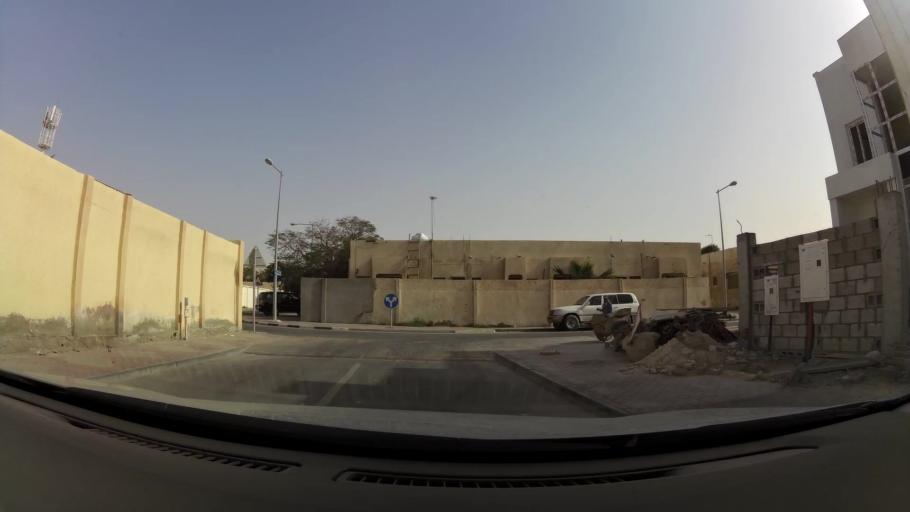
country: QA
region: Baladiyat ar Rayyan
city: Ar Rayyan
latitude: 25.2357
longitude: 51.4405
